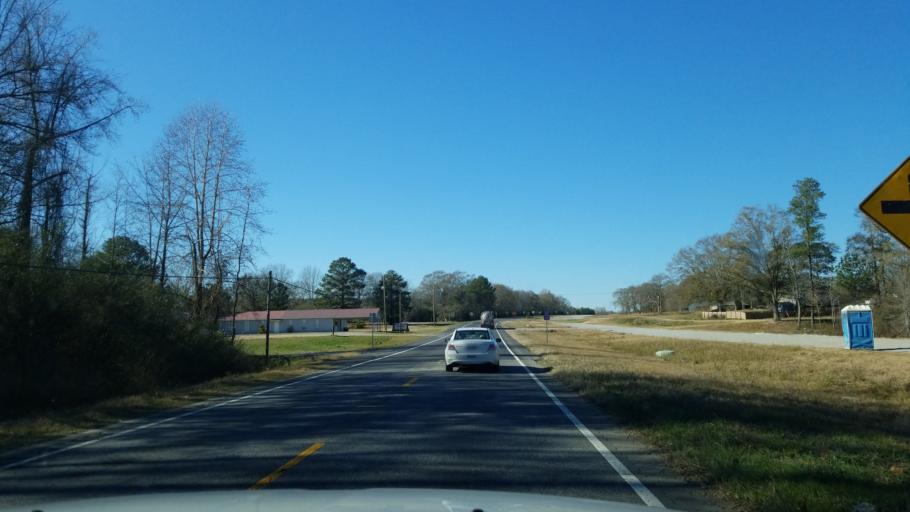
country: US
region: Alabama
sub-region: Pickens County
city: Gordo
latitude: 33.3351
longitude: -87.9277
